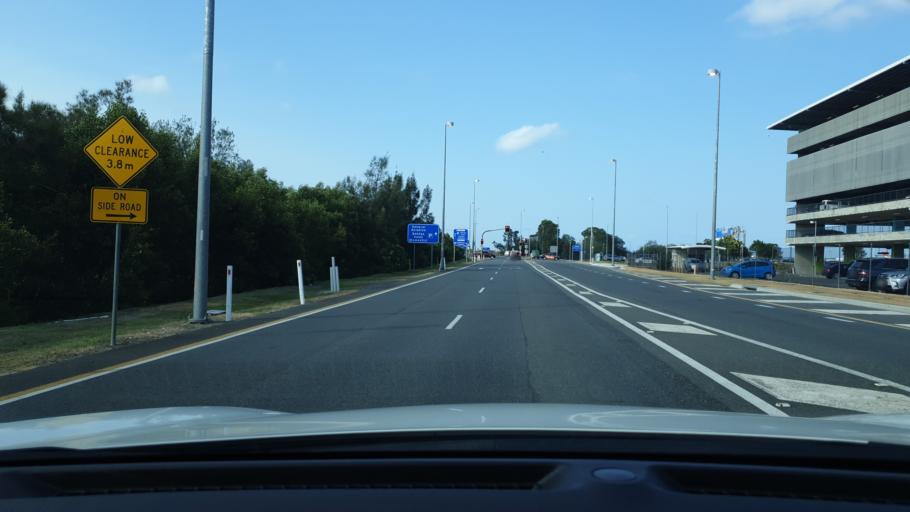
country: AU
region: Queensland
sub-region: Brisbane
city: Shorncliffe
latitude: -27.3836
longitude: 153.1170
